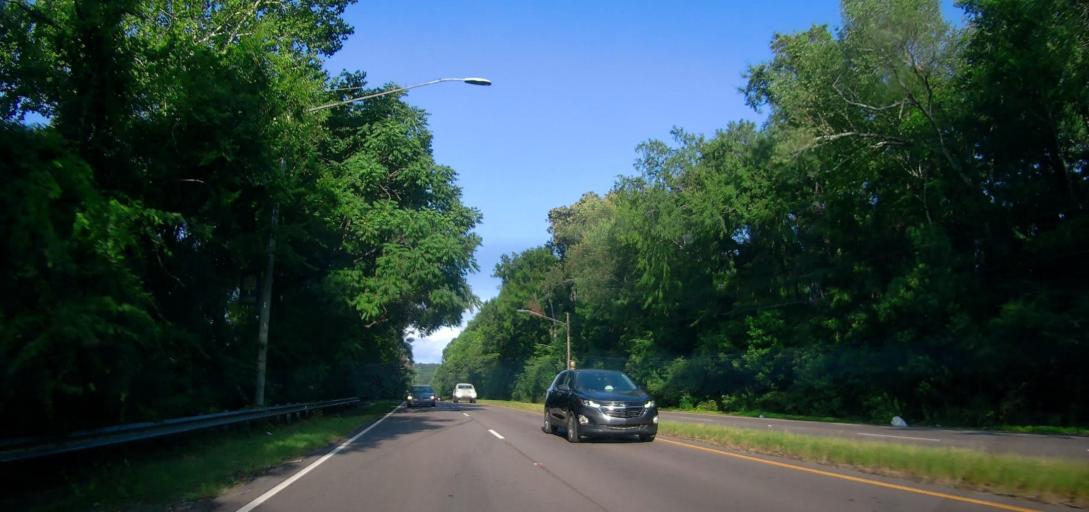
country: US
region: Alabama
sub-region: Jefferson County
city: Mountain Brook
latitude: 33.5277
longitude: -86.7556
